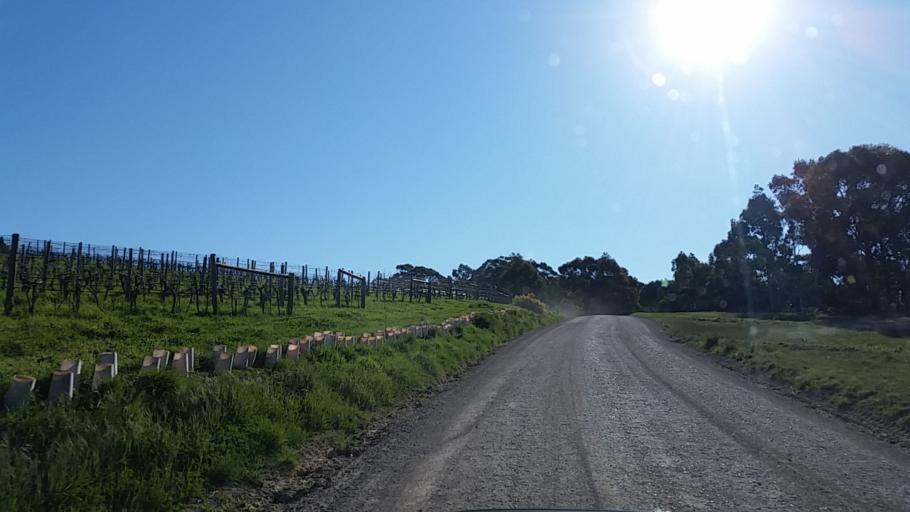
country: AU
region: South Australia
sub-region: Adelaide Hills
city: Lobethal
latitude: -34.8913
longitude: 138.8378
